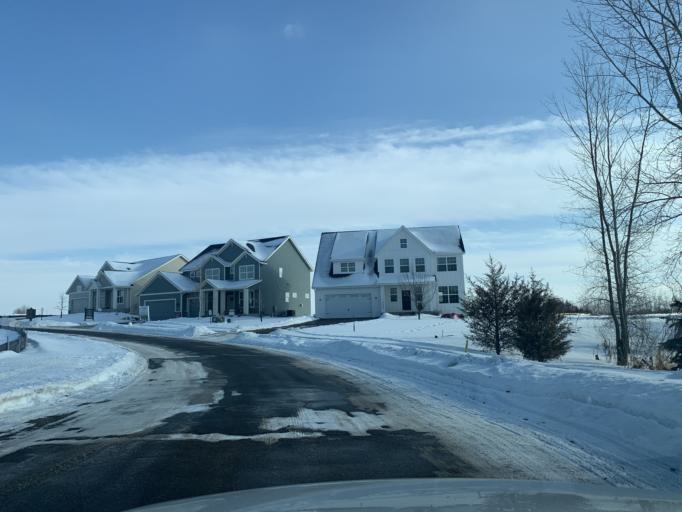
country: US
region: Minnesota
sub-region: Wright County
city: Buffalo
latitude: 45.2033
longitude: -93.8311
